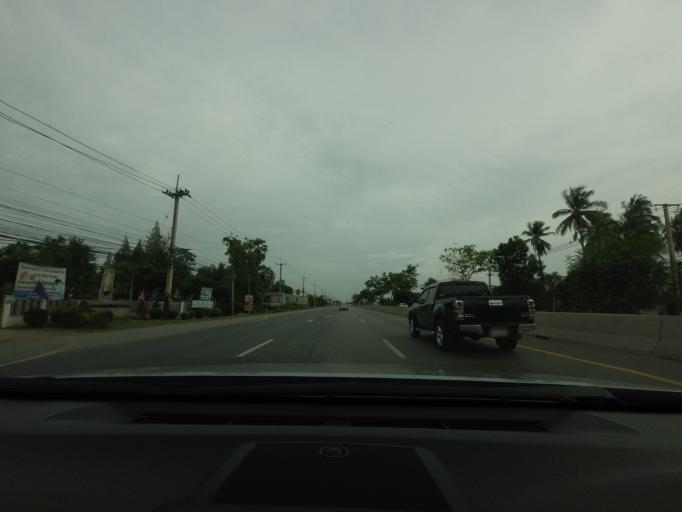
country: TH
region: Phetchaburi
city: Tha Yang
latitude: 12.9302
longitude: 99.9054
